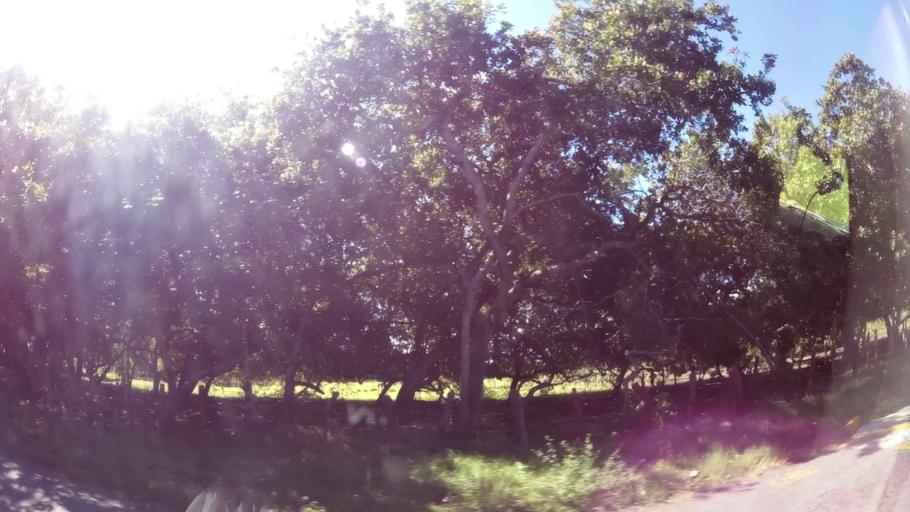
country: GT
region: Santa Rosa
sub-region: Municipio de Taxisco
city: Taxisco
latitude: 13.9085
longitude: -90.5230
